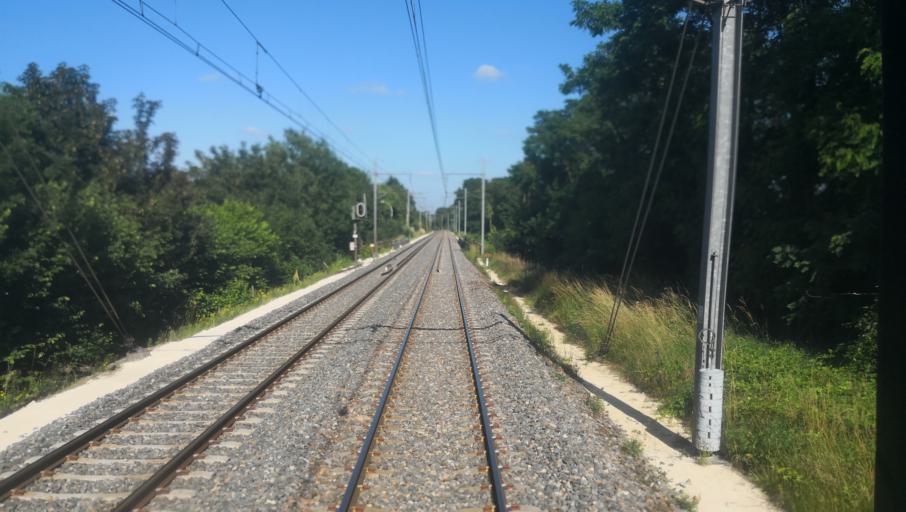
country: FR
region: Ile-de-France
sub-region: Departement de Seine-et-Marne
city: Montigny-sur-Loing
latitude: 48.3363
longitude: 2.7430
